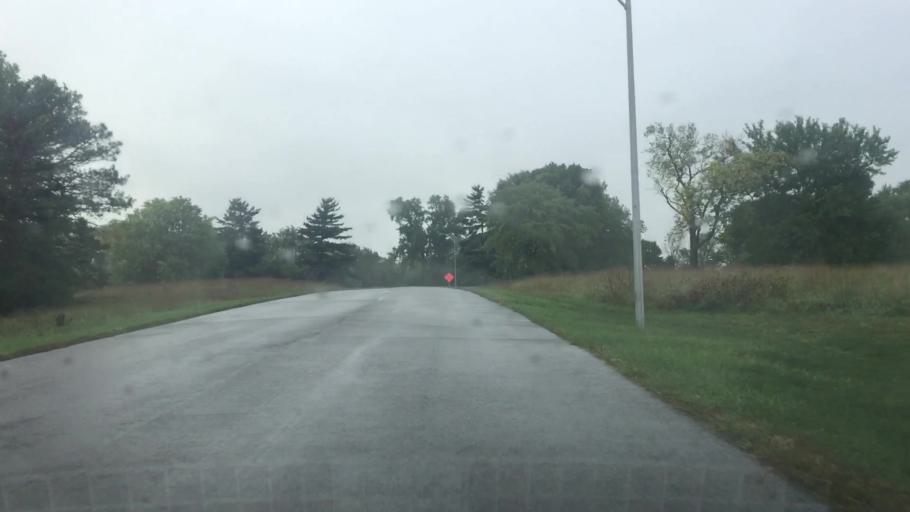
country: US
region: Kansas
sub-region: Johnson County
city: Lenexa
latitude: 38.9768
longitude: -94.8082
